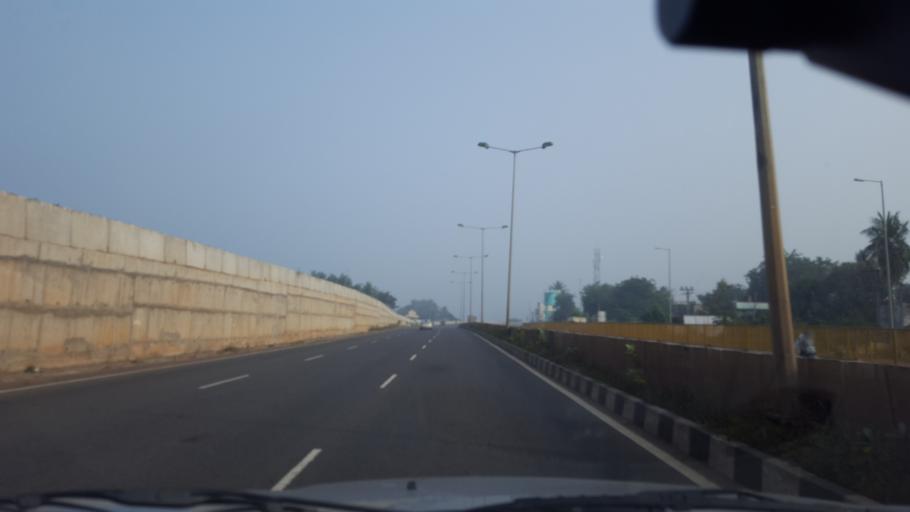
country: IN
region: Andhra Pradesh
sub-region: Prakasam
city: Ongole
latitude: 15.4209
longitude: 80.0393
